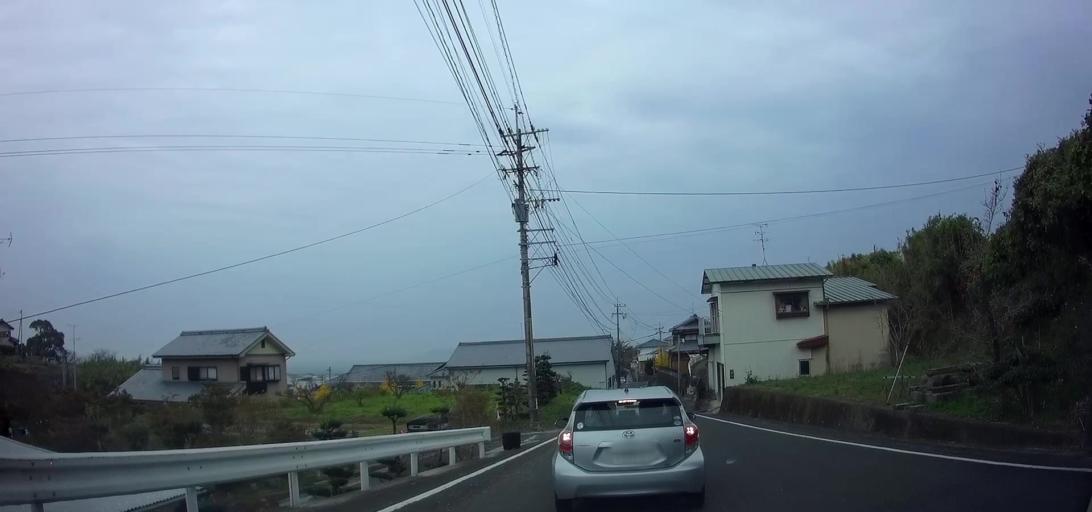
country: JP
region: Nagasaki
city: Shimabara
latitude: 32.6609
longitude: 130.2887
